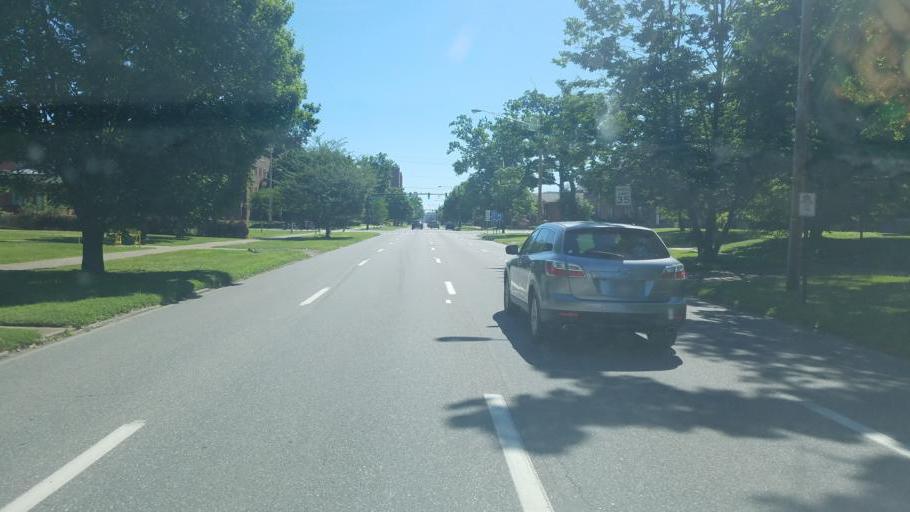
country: US
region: West Virginia
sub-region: Cabell County
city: Huntington
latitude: 38.4213
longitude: -82.4327
